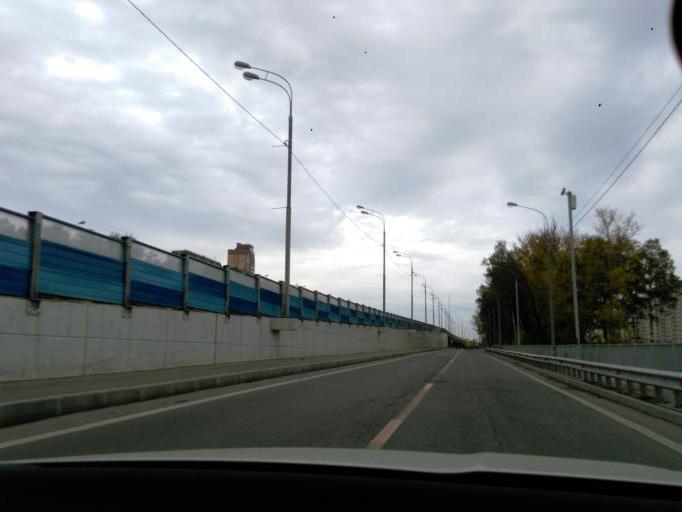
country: RU
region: Moscow
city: Severnyy
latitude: 55.9352
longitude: 37.5457
